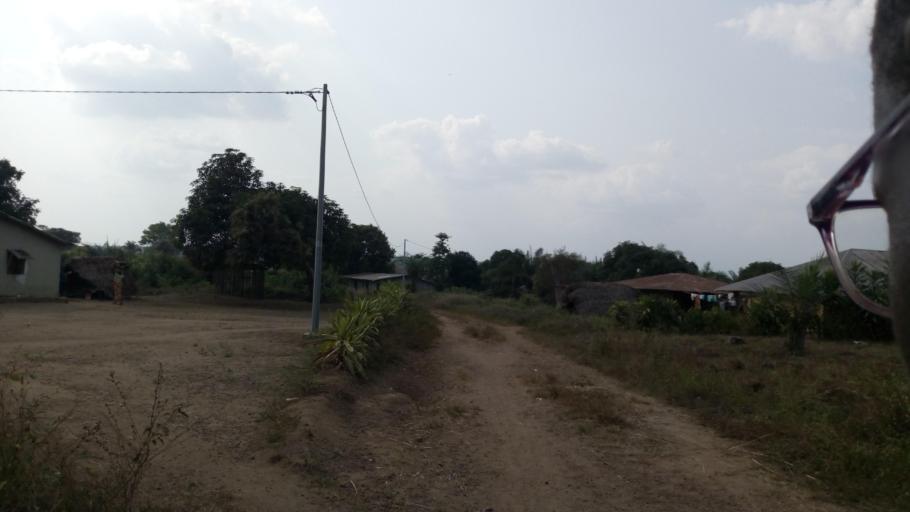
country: SL
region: Southern Province
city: Mogbwemo
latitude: 7.7653
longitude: -12.3148
